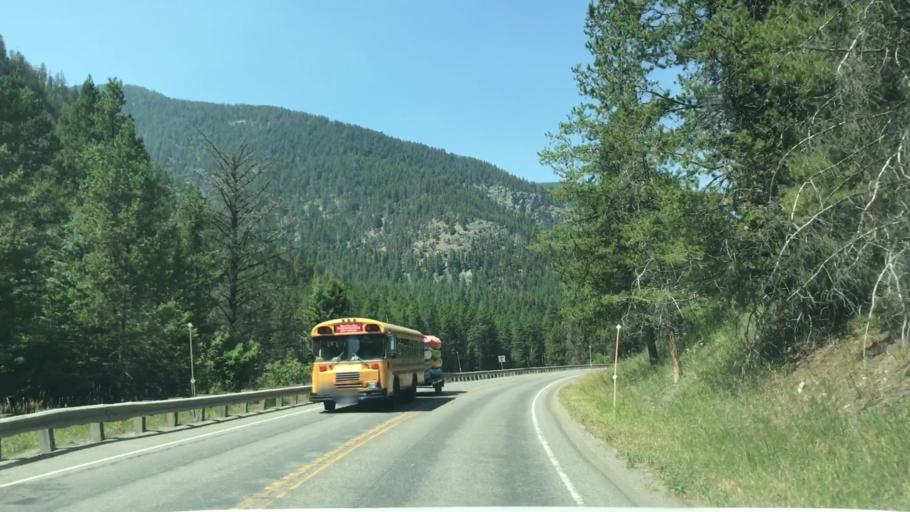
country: US
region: Montana
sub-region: Gallatin County
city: Big Sky
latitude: 45.3984
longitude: -111.2149
